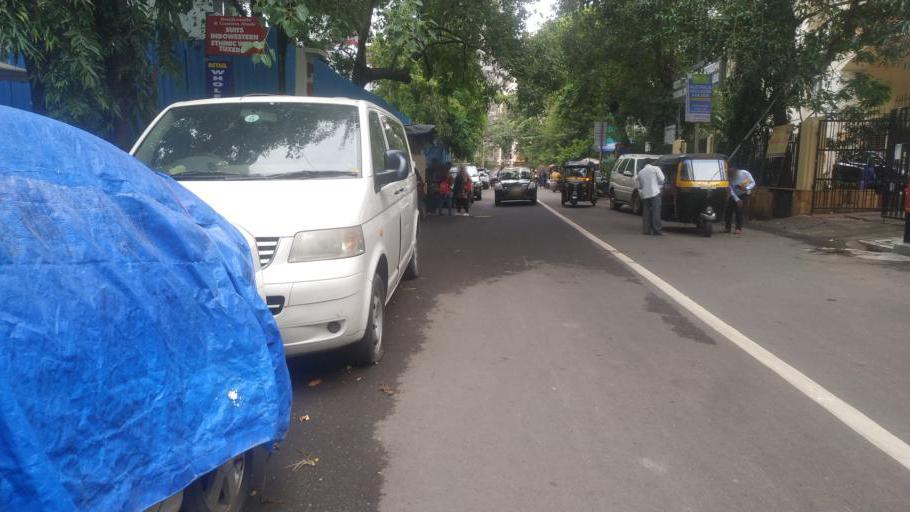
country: IN
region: Maharashtra
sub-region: Mumbai Suburban
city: Mumbai
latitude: 19.0648
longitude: 72.8362
